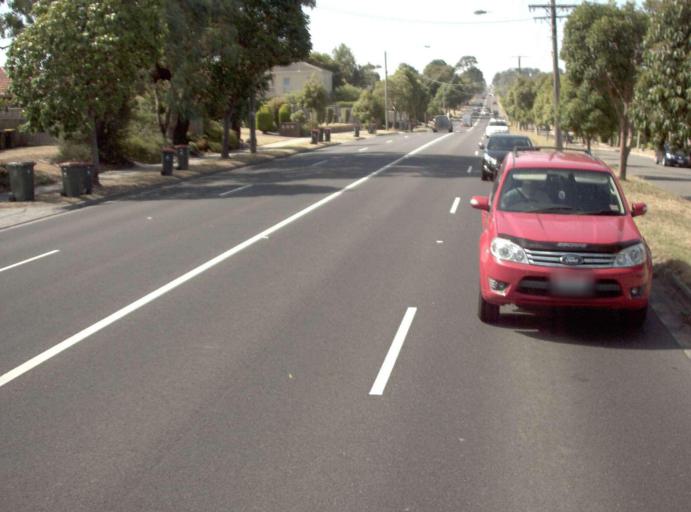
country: AU
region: Victoria
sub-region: Monash
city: Mulgrave
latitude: -37.9204
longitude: 145.1866
